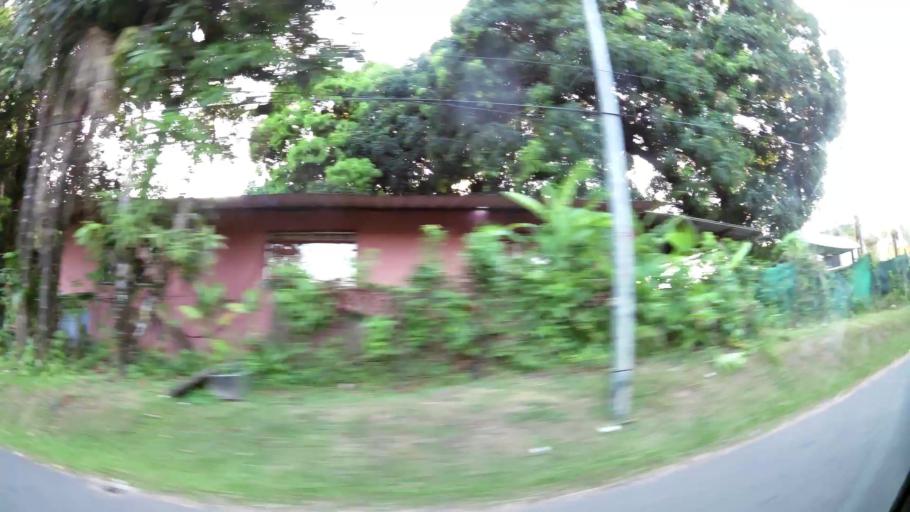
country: GF
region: Guyane
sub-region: Guyane
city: Cayenne
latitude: 4.9248
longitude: -52.3036
